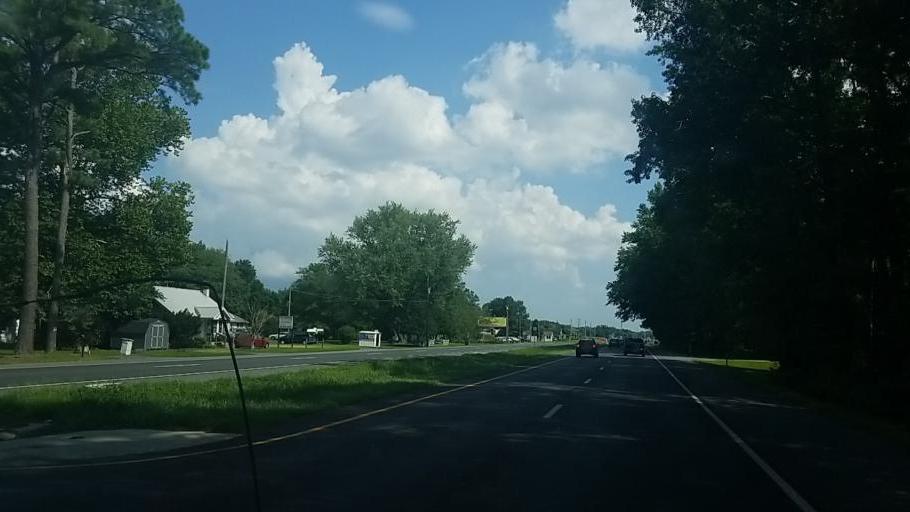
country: US
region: Delaware
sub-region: Sussex County
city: Millsboro
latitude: 38.5495
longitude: -75.2641
